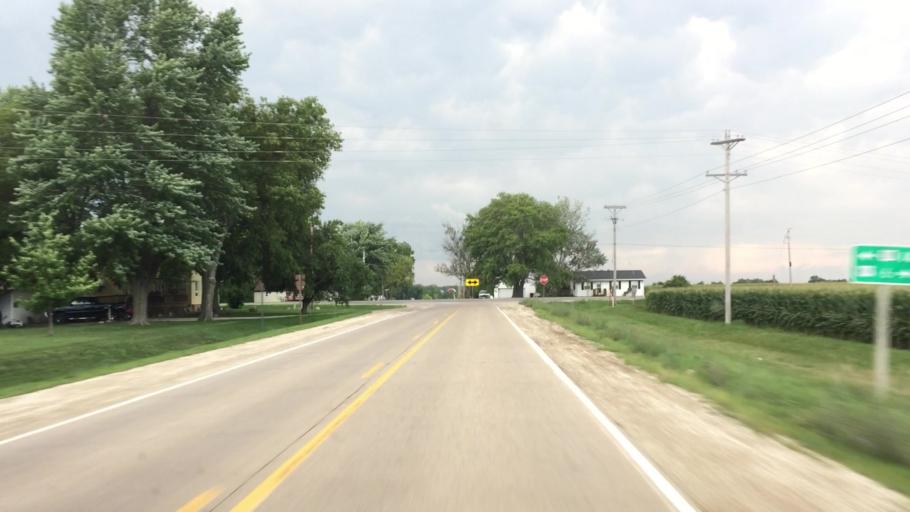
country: US
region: Iowa
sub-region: Lee County
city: Fort Madison
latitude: 40.7407
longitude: -91.3281
